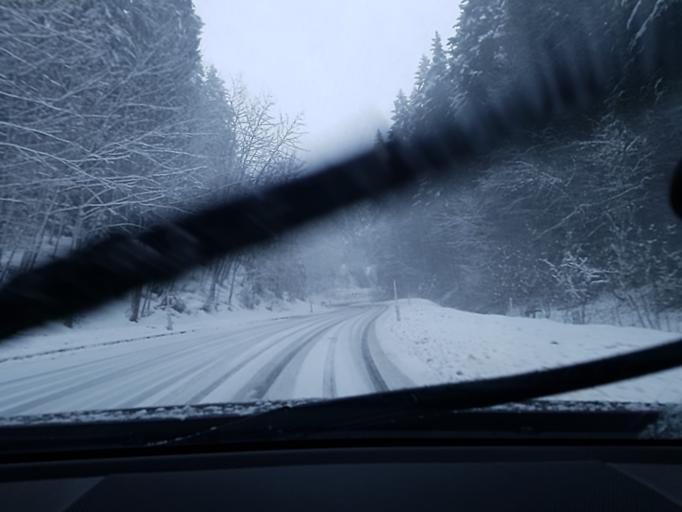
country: AT
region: Salzburg
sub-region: Politischer Bezirk Hallein
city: Abtenau
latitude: 47.5660
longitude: 13.3797
